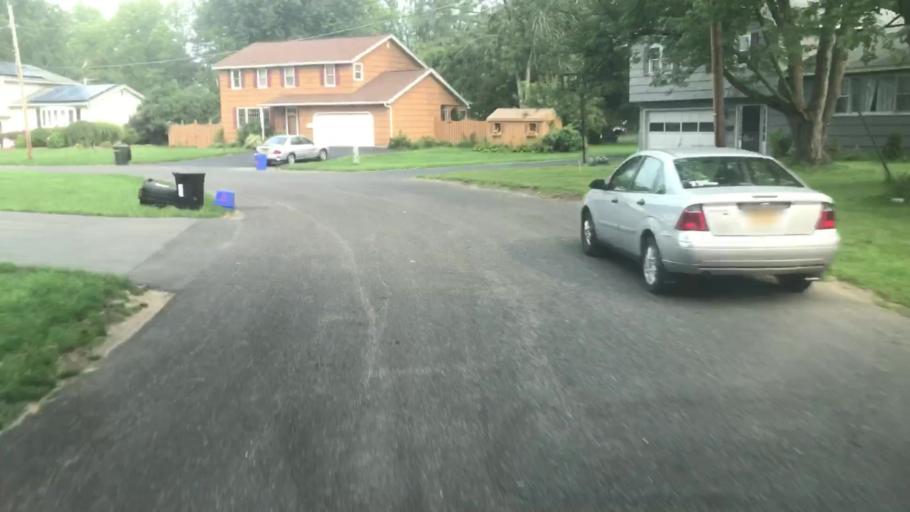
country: US
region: New York
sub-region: Onondaga County
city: Liverpool
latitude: 43.1364
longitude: -76.2203
